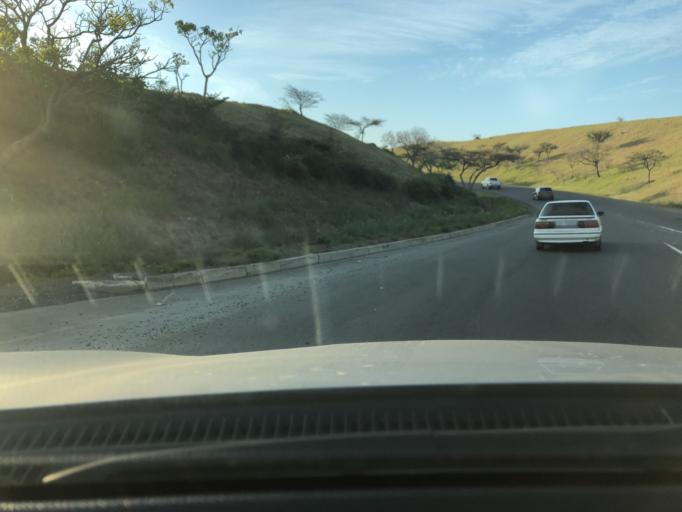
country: ZA
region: KwaZulu-Natal
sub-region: iLembe District Municipality
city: Ballitoville
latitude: -29.6207
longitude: 31.0917
